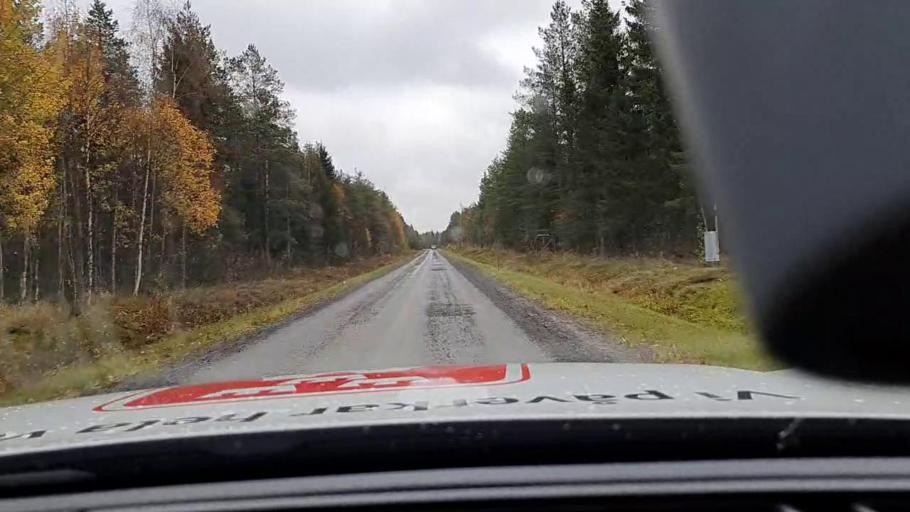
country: SE
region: Norrbotten
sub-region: Haparanda Kommun
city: Haparanda
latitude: 65.9601
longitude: 23.9285
